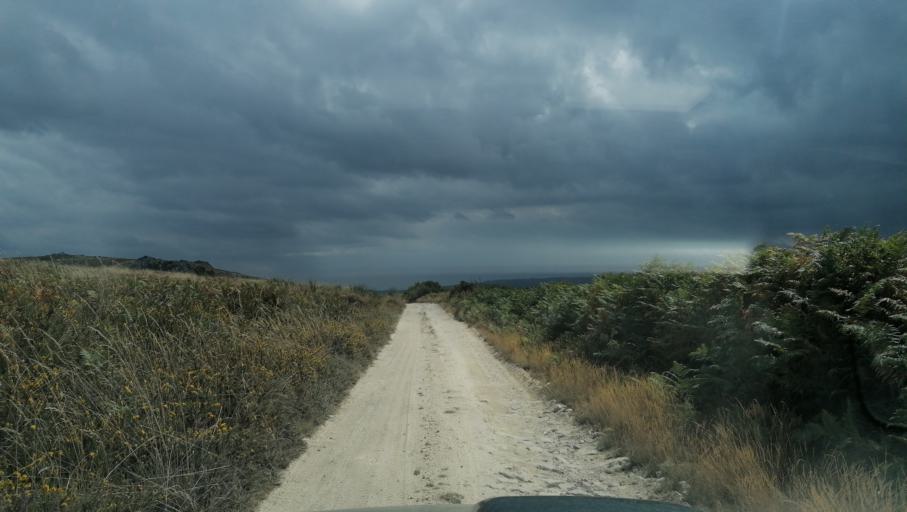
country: PT
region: Vila Real
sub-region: Vila Pouca de Aguiar
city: Vila Pouca de Aguiar
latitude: 41.5360
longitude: -7.6994
